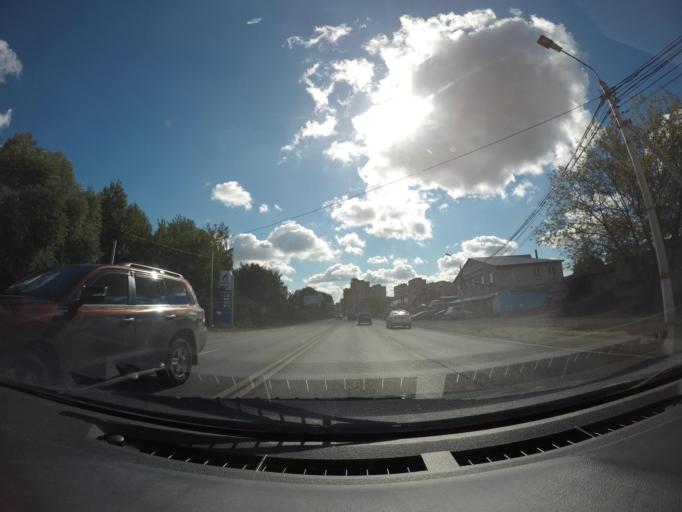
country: RU
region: Moskovskaya
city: Ramenskoye
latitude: 55.5843
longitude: 38.2389
